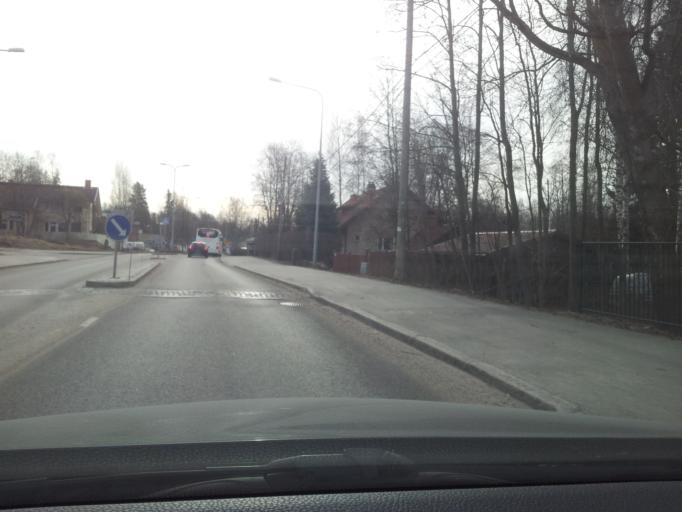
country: FI
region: Uusimaa
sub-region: Helsinki
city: Kilo
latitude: 60.1914
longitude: 24.7756
